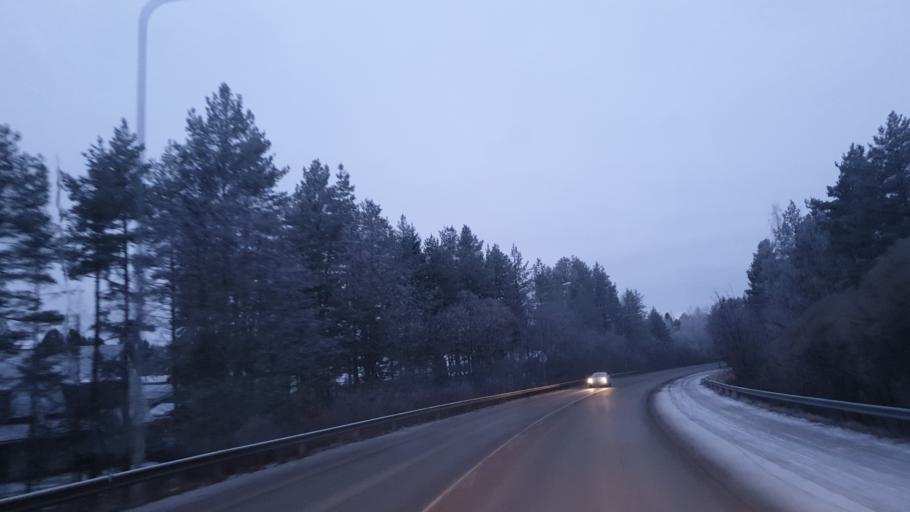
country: FI
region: Southern Ostrobothnia
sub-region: Seinaejoki
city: Nurmo
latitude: 62.7733
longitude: 22.8857
